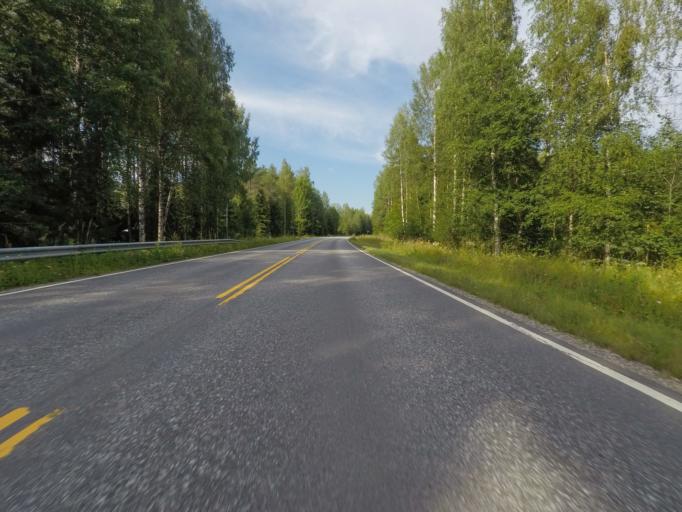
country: FI
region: Southern Savonia
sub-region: Savonlinna
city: Sulkava
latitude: 61.9027
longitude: 28.5849
